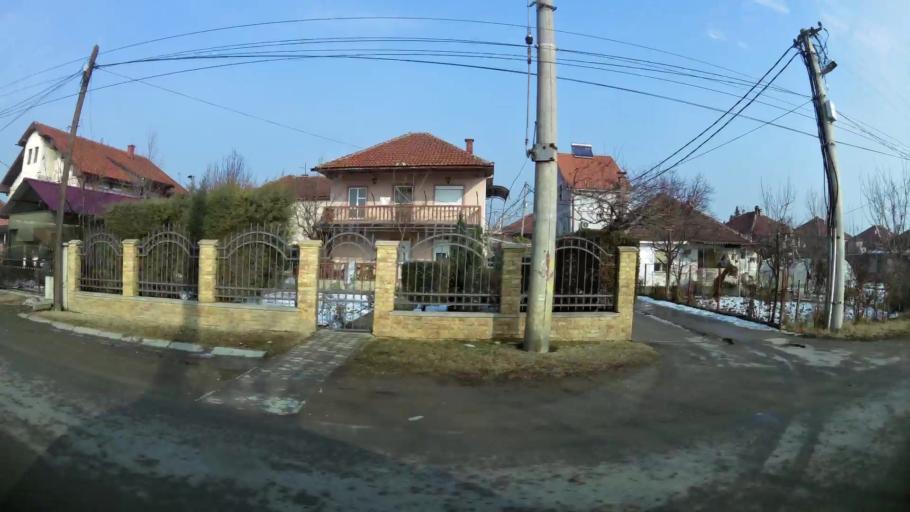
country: MK
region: Ilinden
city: Marino
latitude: 41.9875
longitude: 21.5883
